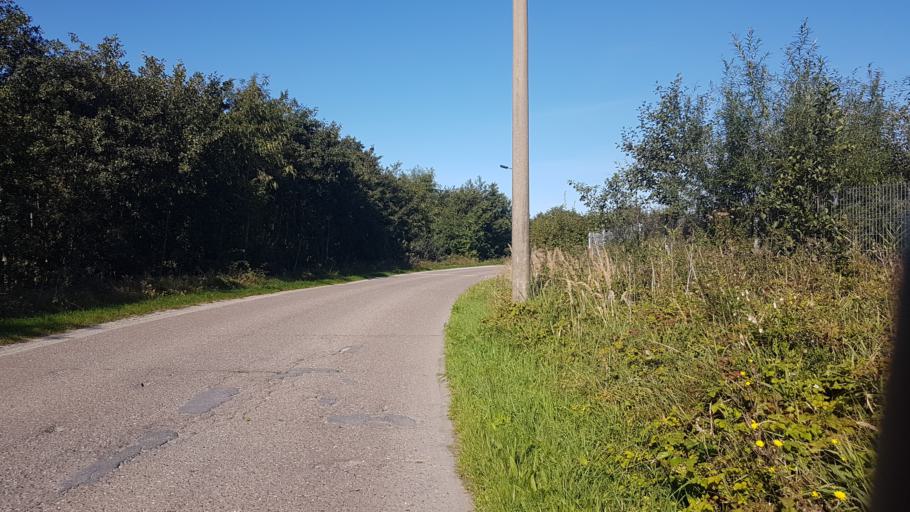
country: DE
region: Mecklenburg-Vorpommern
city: Sagard
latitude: 54.4950
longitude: 13.5536
